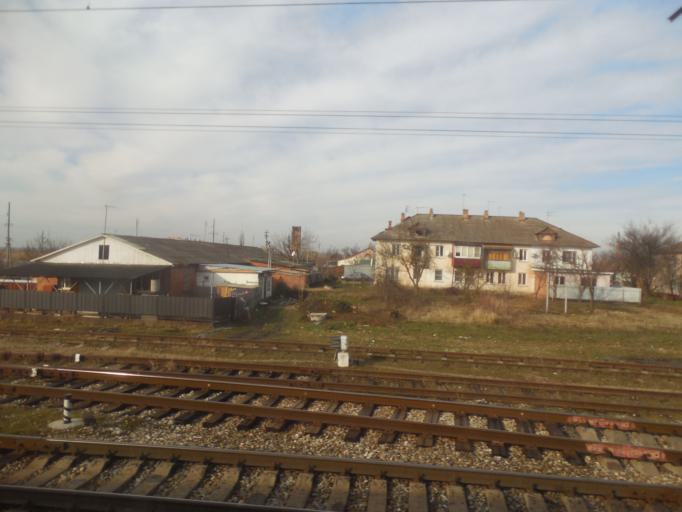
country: RU
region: Adygeya
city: Enem
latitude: 44.9249
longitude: 38.9030
